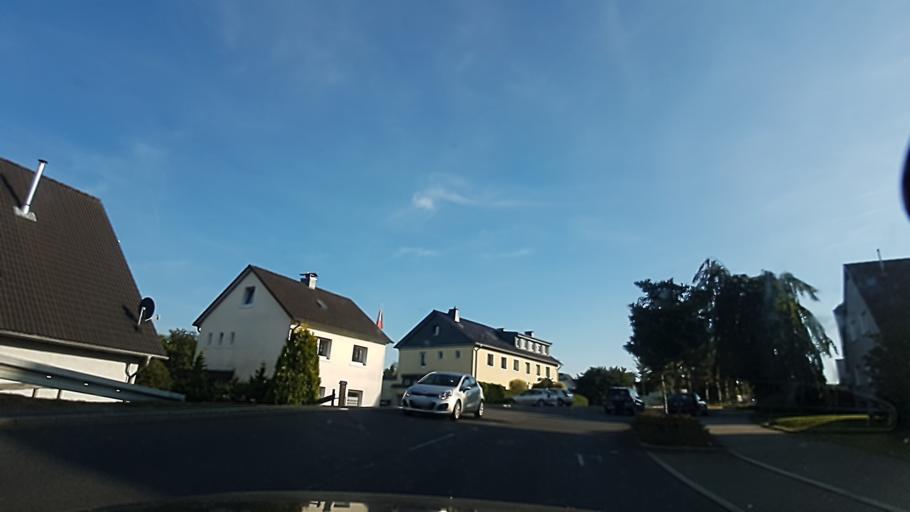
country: DE
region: North Rhine-Westphalia
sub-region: Regierungsbezirk Koln
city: Marienheide
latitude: 51.0827
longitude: 7.5359
